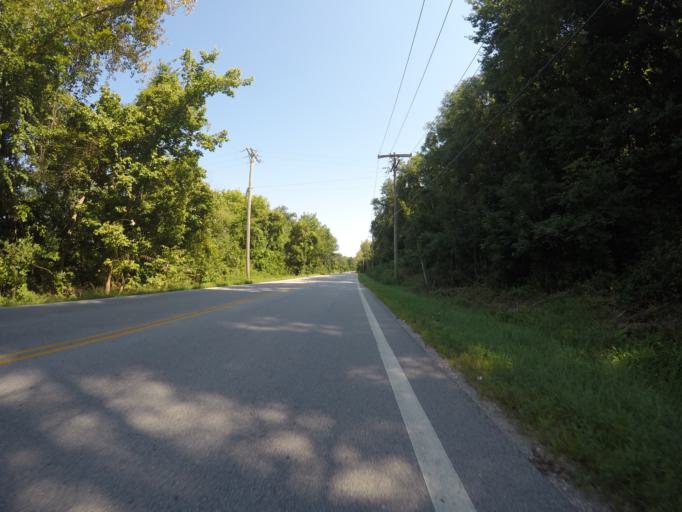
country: US
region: Kansas
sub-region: Leavenworth County
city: Lansing
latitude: 39.2003
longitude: -94.8171
